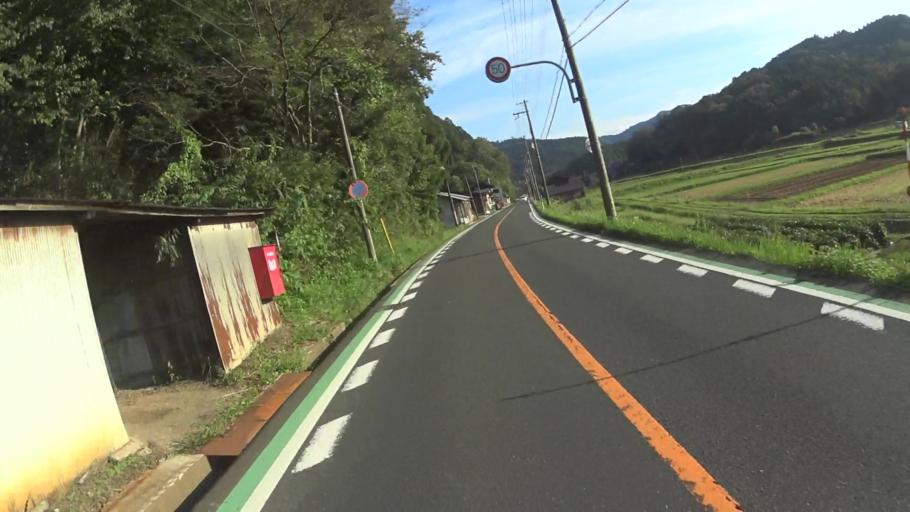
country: JP
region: Hyogo
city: Toyooka
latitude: 35.5978
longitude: 134.9049
